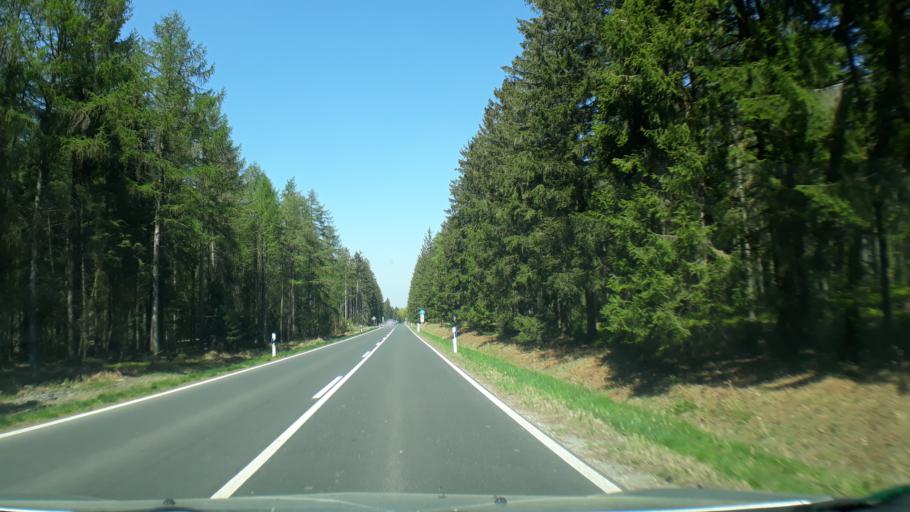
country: DE
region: North Rhine-Westphalia
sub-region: Regierungsbezirk Koln
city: Roetgen
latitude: 50.6629
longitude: 6.2473
